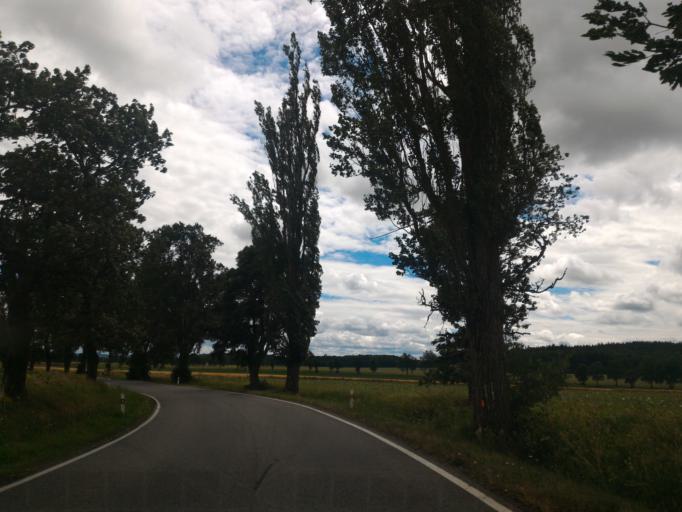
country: CZ
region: Vysocina
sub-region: Okres Jihlava
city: Telc
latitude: 49.2046
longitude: 15.4333
